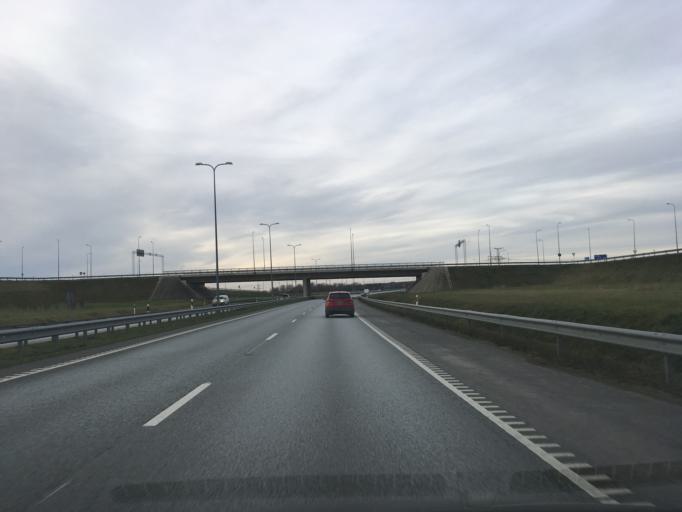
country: EE
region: Ida-Virumaa
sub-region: Johvi vald
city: Johvi
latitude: 59.3859
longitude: 27.3503
